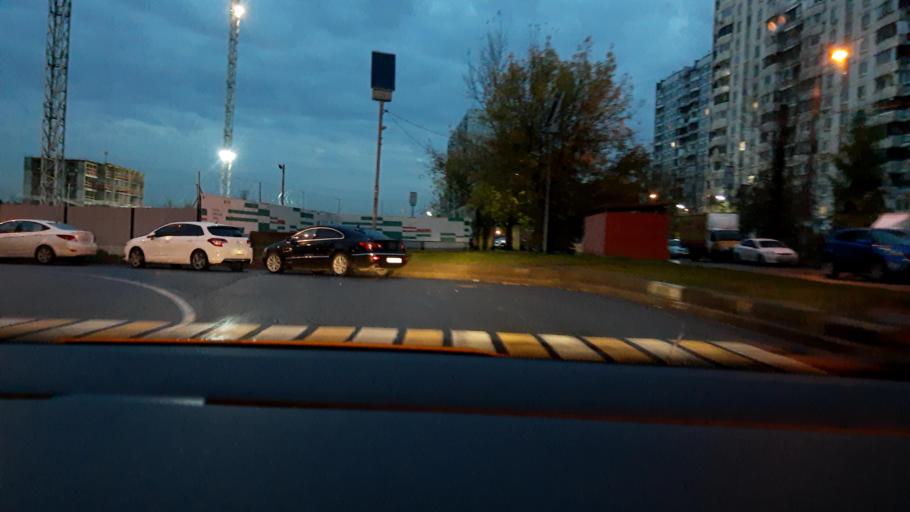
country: RU
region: Moscow
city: Vostochnyy
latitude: 55.8203
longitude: 37.8736
